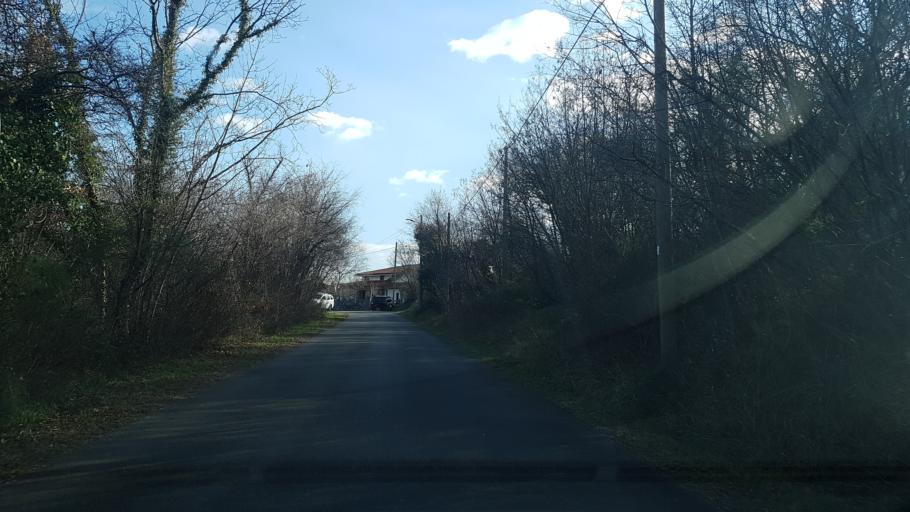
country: IT
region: Friuli Venezia Giulia
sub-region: Provincia di Gorizia
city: Doberdo del Lago
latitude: 45.8763
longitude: 13.5308
